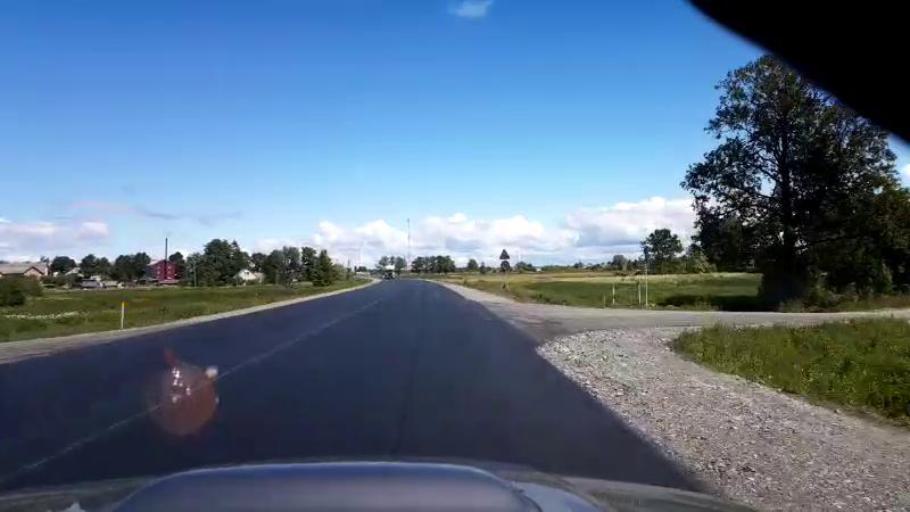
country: LV
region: Salacgrivas
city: Ainazi
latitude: 57.8565
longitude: 24.3648
